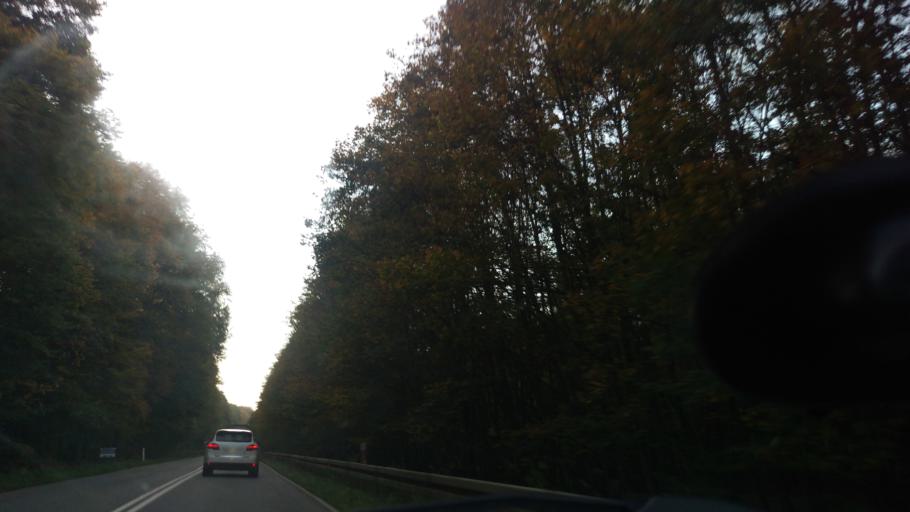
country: PL
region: West Pomeranian Voivodeship
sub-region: Powiat gryfinski
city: Stare Czarnowo
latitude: 53.3321
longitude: 14.7760
